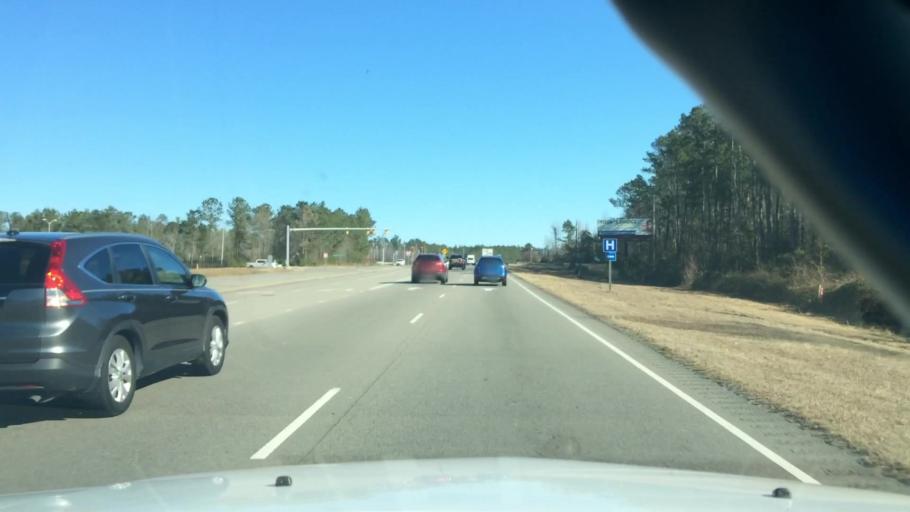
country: US
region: North Carolina
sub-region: Brunswick County
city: Bolivia
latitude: 34.0303
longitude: -78.2580
